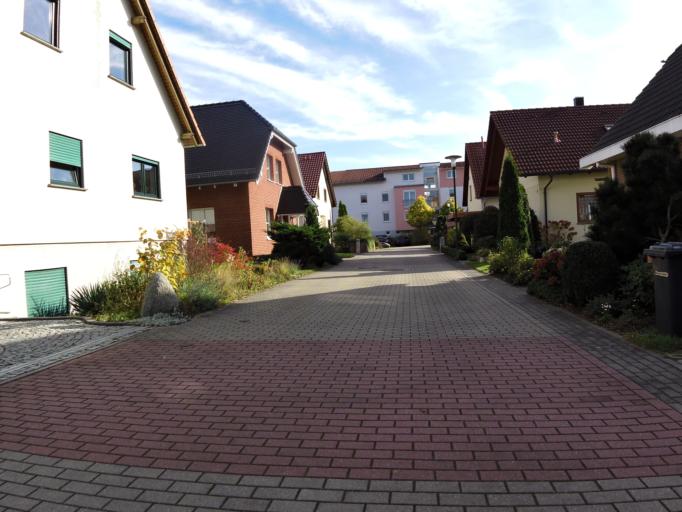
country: DE
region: Saxony
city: Markkleeberg
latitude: 51.3022
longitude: 12.4342
